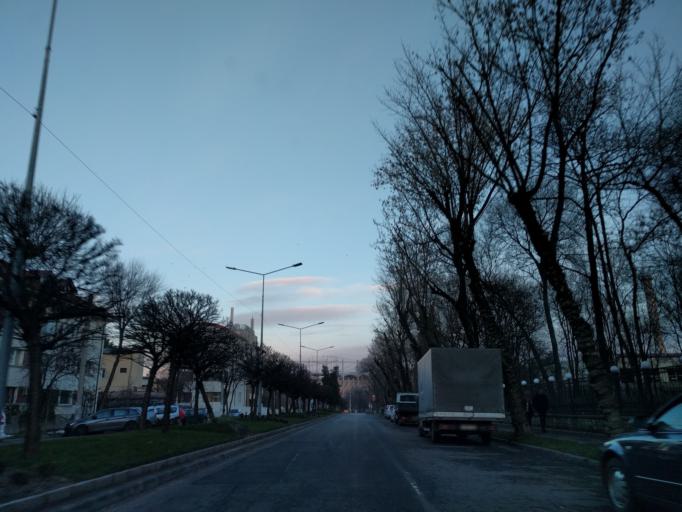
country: RO
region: Ilfov
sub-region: Comuna Fundeni-Dobroesti
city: Fundeni
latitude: 44.4362
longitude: 26.1447
